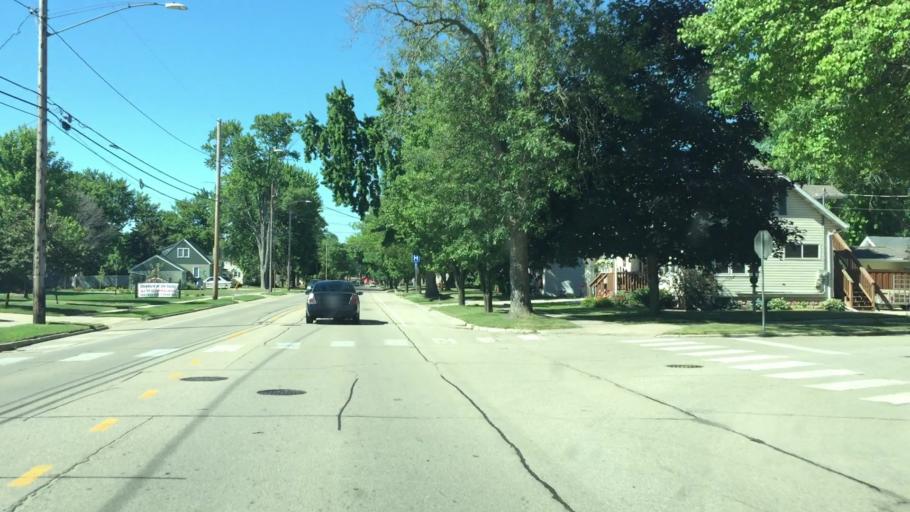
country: US
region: Wisconsin
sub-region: Winnebago County
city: Menasha
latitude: 44.2146
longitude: -88.4339
